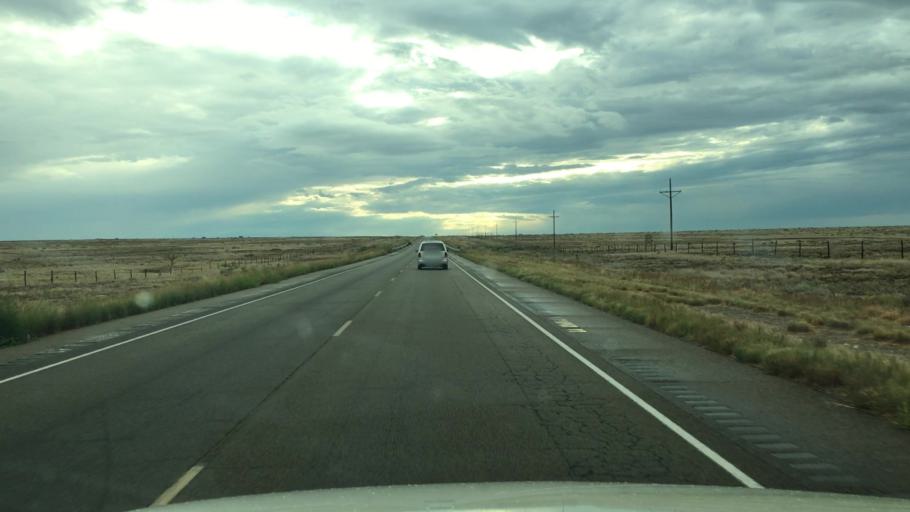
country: US
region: New Mexico
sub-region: Chaves County
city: Roswell
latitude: 33.4040
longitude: -104.3183
